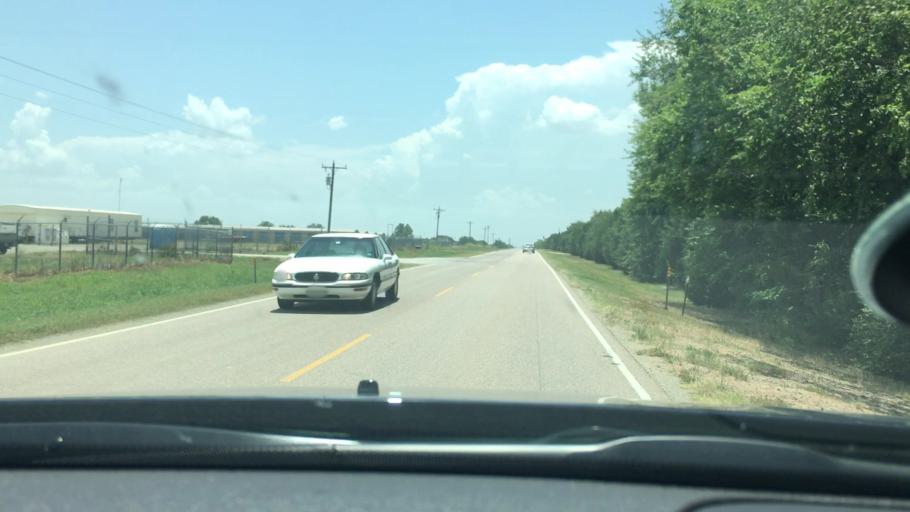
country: US
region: Oklahoma
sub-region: Johnston County
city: Tishomingo
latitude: 34.2833
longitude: -96.6711
